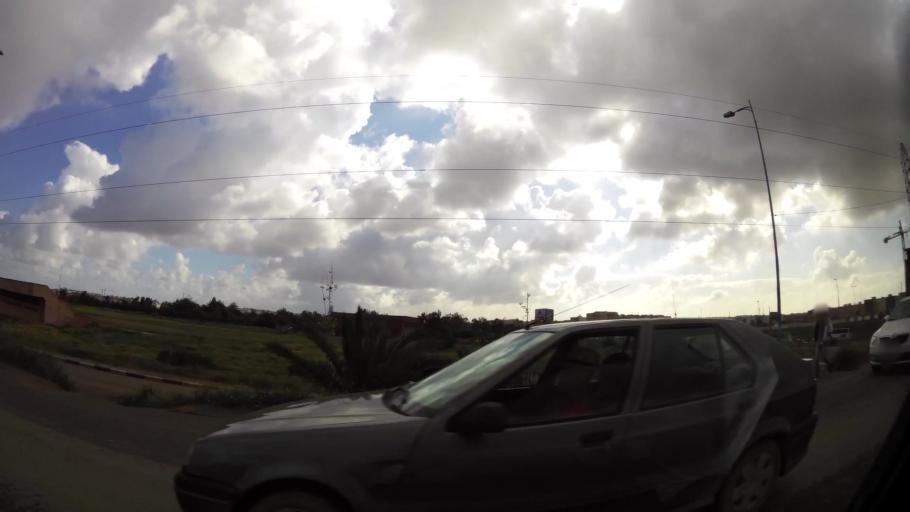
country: MA
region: Grand Casablanca
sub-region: Mediouna
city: Tit Mellil
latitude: 33.5921
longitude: -7.5286
